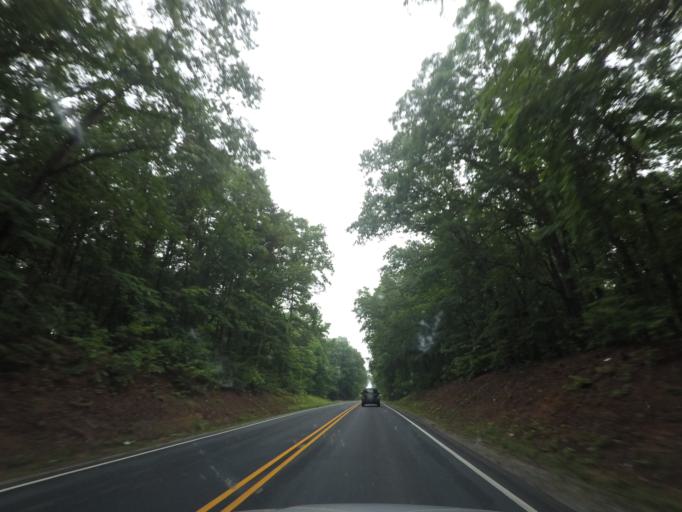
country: US
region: Virginia
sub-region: Prince Edward County
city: Hampden Sydney
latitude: 37.0799
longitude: -78.4761
